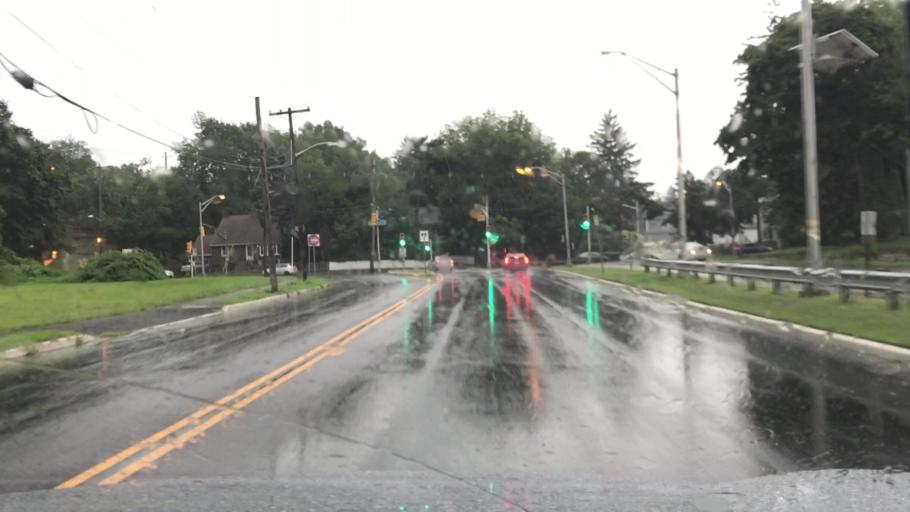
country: US
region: New Jersey
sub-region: Bergen County
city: Teaneck
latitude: 40.8995
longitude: -74.0281
